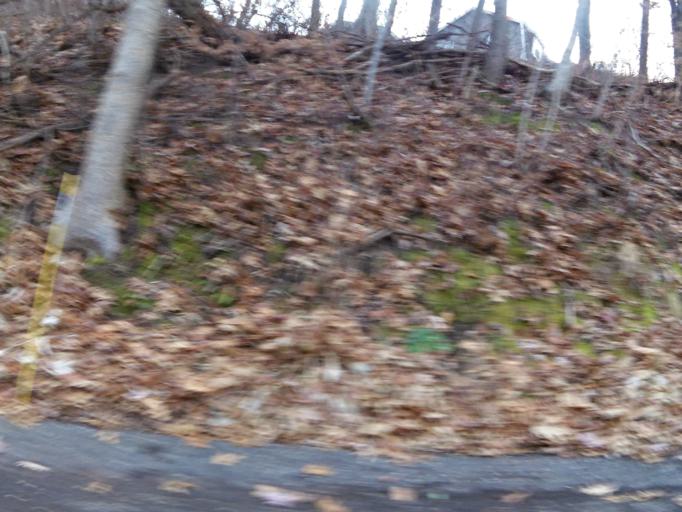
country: US
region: Wisconsin
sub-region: Saint Croix County
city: North Hudson
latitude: 44.9860
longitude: -92.7492
